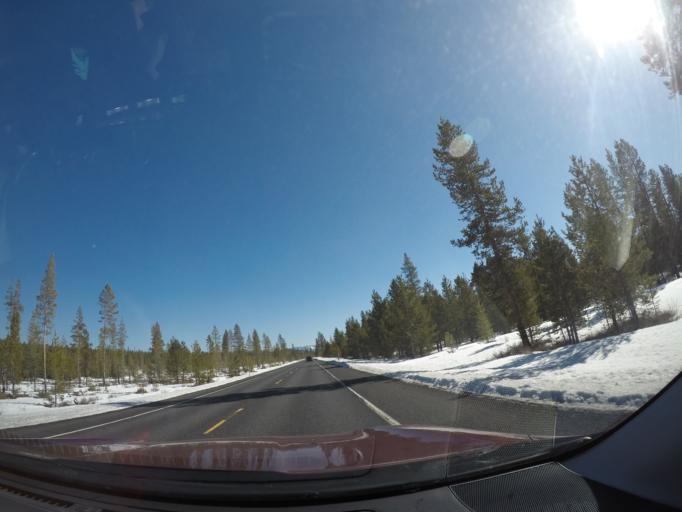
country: US
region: Oregon
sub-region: Deschutes County
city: Three Rivers
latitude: 43.8647
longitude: -121.5375
